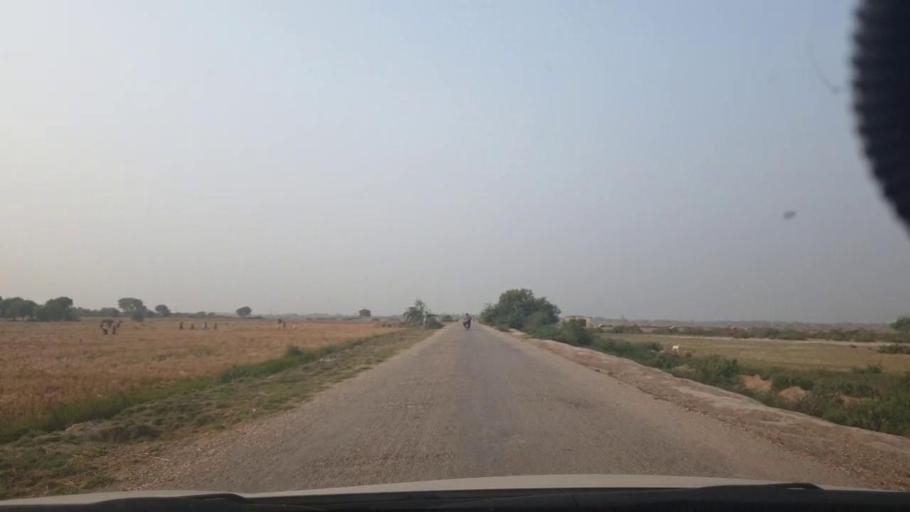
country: PK
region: Sindh
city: Bulri
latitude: 24.8129
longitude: 68.4078
